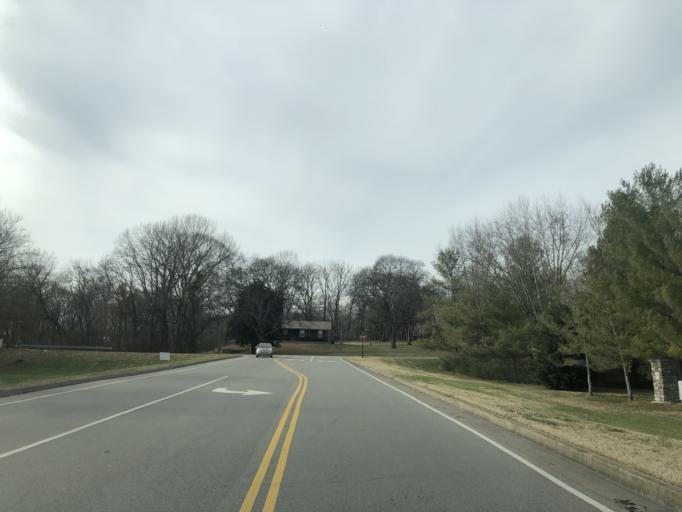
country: US
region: Tennessee
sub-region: Williamson County
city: Franklin
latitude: 35.9686
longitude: -86.8994
